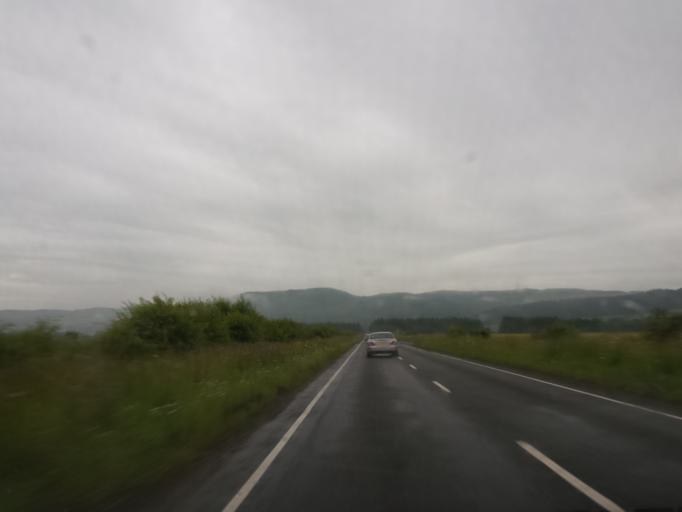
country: GB
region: Scotland
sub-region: Perth and Kinross
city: Bridge of Earn
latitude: 56.3369
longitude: -3.3822
